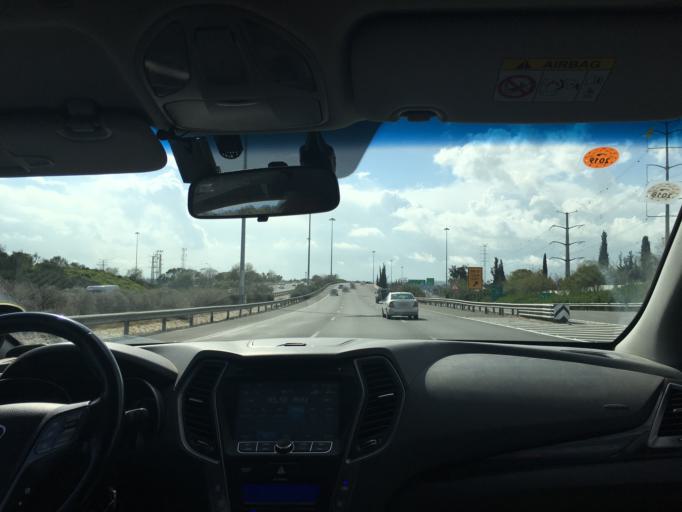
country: IL
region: Tel Aviv
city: Azor
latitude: 32.0418
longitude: 34.8295
